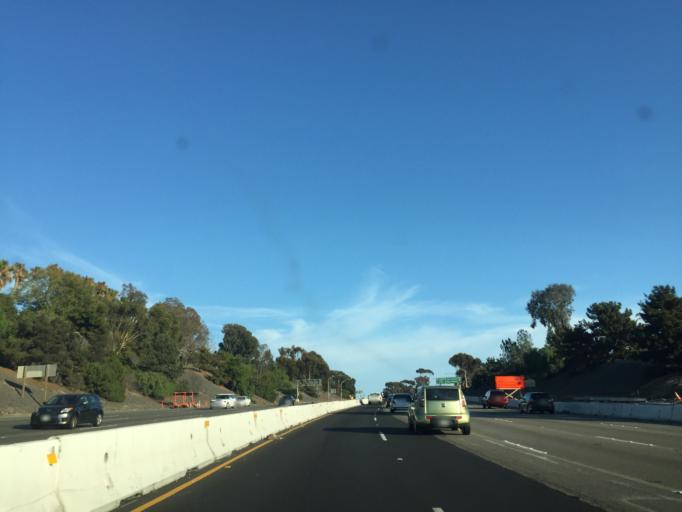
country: US
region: California
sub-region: Orange County
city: San Clemente
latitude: 33.4361
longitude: -117.6183
